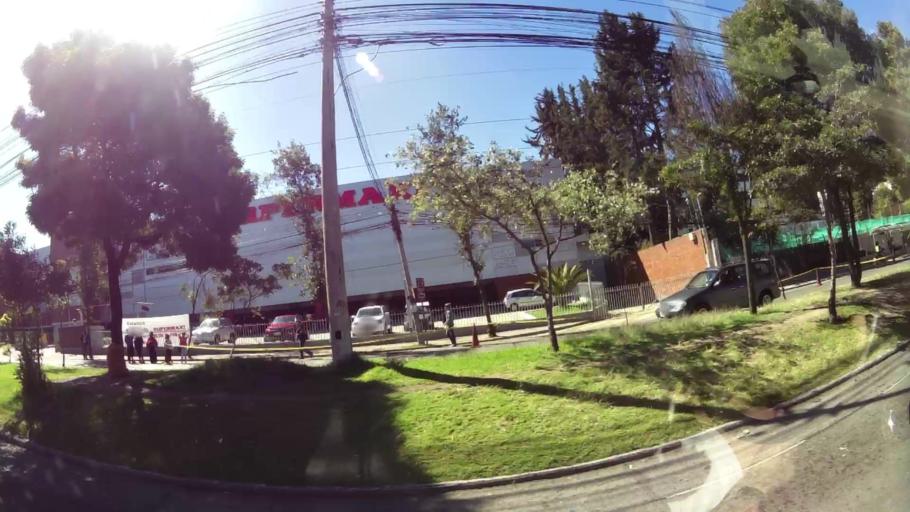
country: EC
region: Pichincha
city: Quito
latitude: -0.1642
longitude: -78.4679
